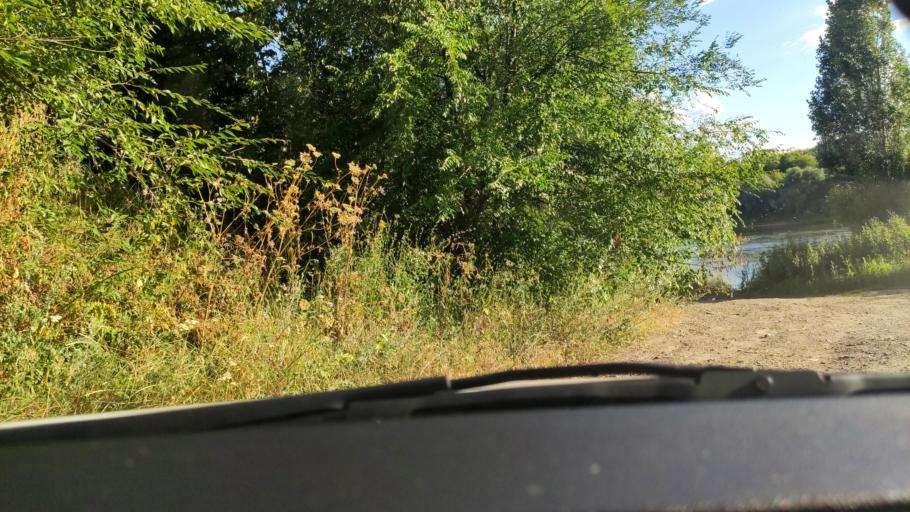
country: RU
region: Voronezj
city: Semiluki
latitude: 51.6828
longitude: 39.0474
